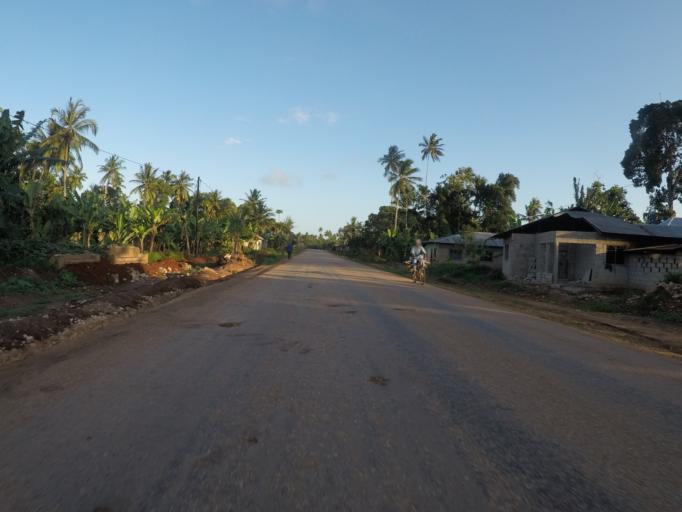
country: TZ
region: Zanzibar North
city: Gamba
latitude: -5.8952
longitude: 39.2920
